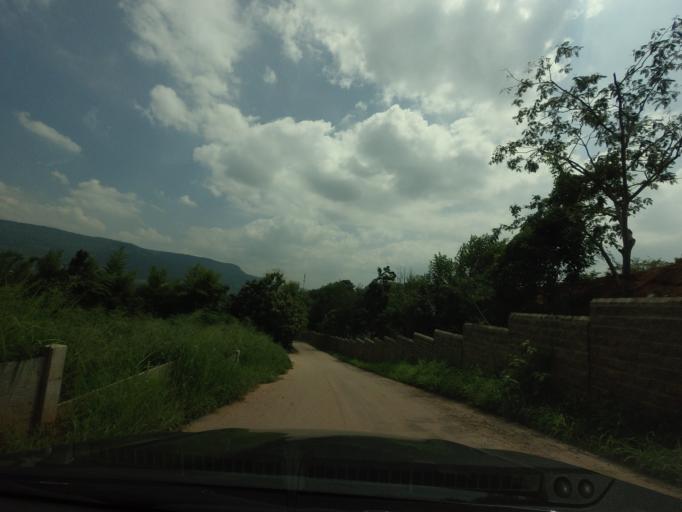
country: TH
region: Loei
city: Phu Ruea
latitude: 17.4551
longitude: 101.3510
